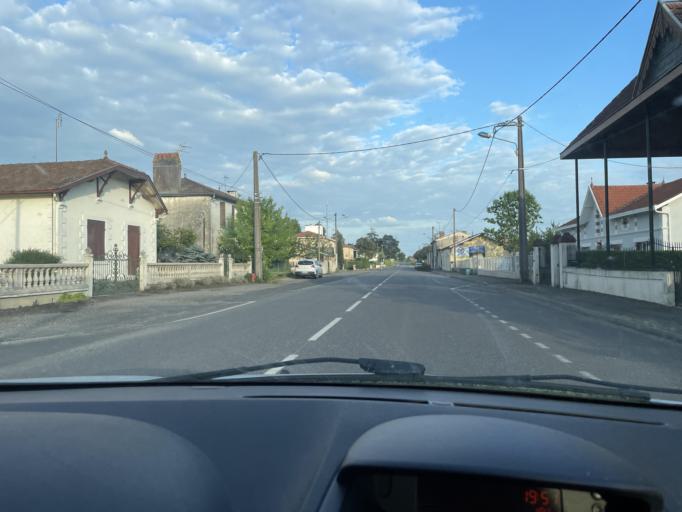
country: FR
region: Aquitaine
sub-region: Departement de la Gironde
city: Grignols
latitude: 44.3862
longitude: -0.0426
